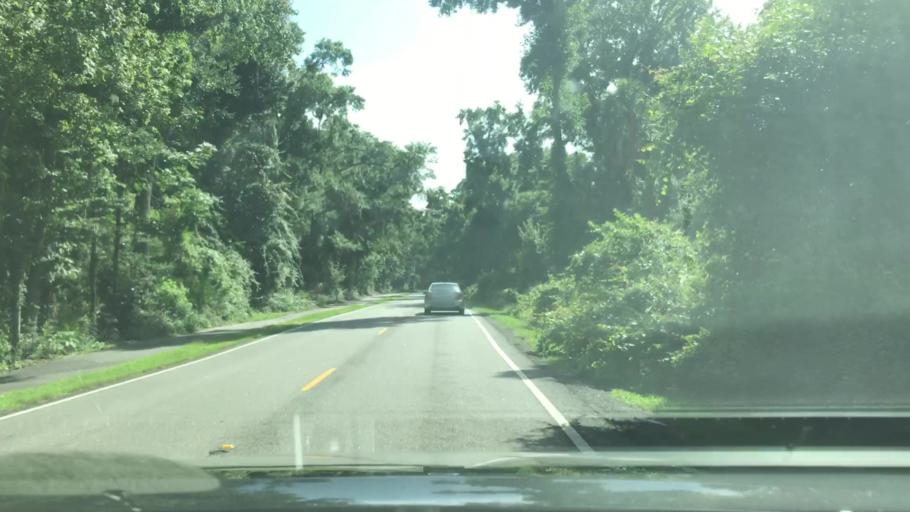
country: US
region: South Carolina
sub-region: Beaufort County
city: Hilton Head Island
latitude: 32.1391
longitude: -80.7687
